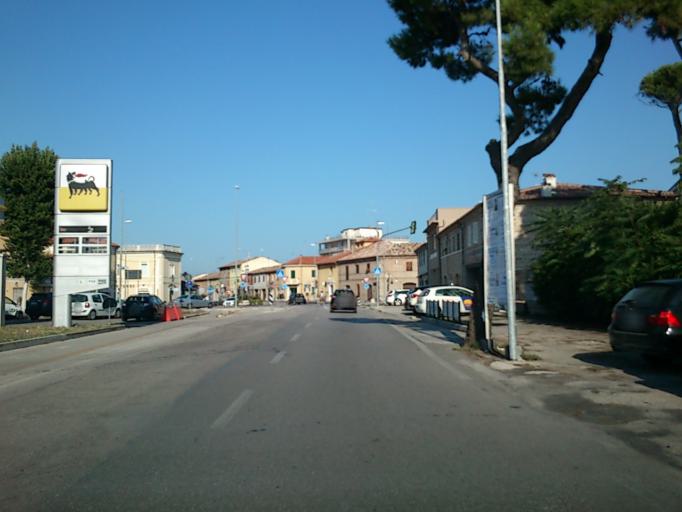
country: IT
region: The Marches
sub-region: Provincia di Pesaro e Urbino
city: Fano
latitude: 43.8397
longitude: 13.0185
